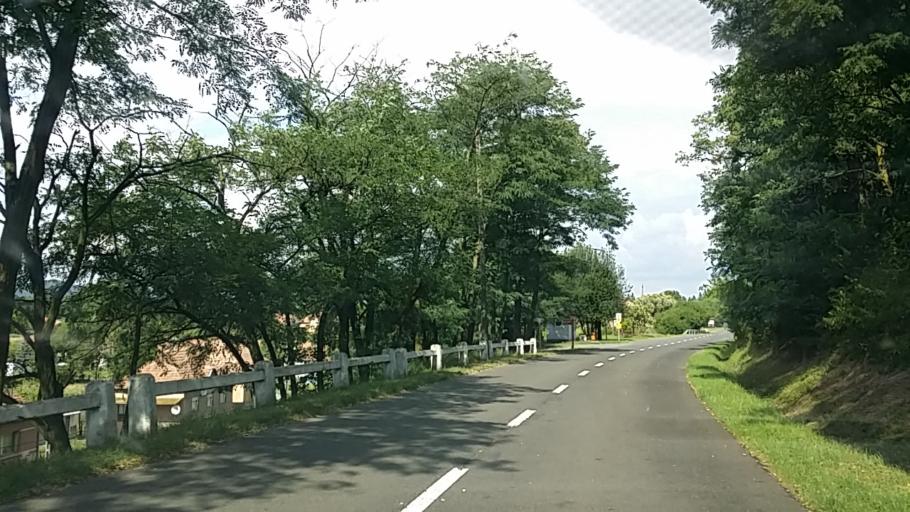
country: SK
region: Nitriansky
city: Sahy
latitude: 48.0519
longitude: 19.0003
